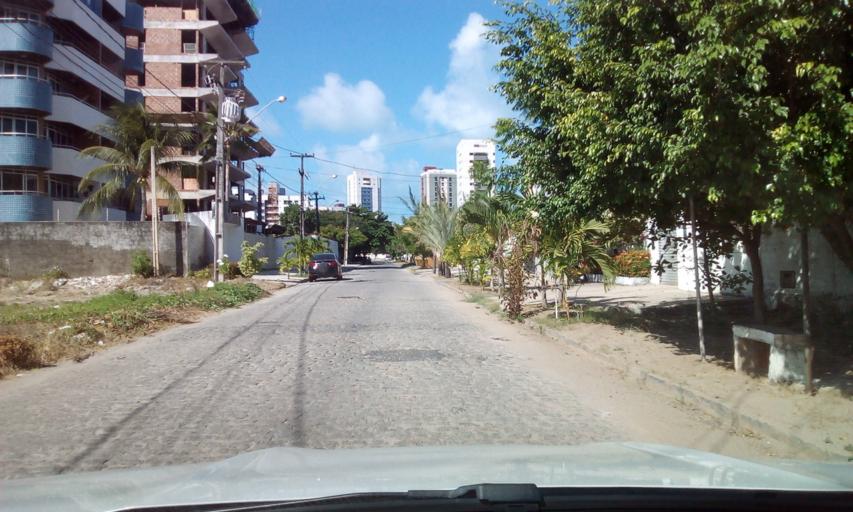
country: BR
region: Paraiba
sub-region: Joao Pessoa
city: Joao Pessoa
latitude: -7.0812
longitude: -34.8336
